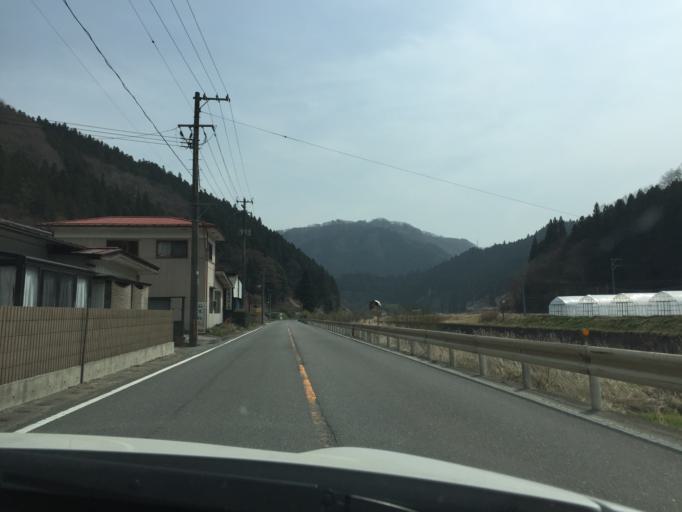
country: JP
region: Fukushima
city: Ishikawa
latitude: 37.0650
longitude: 140.5836
